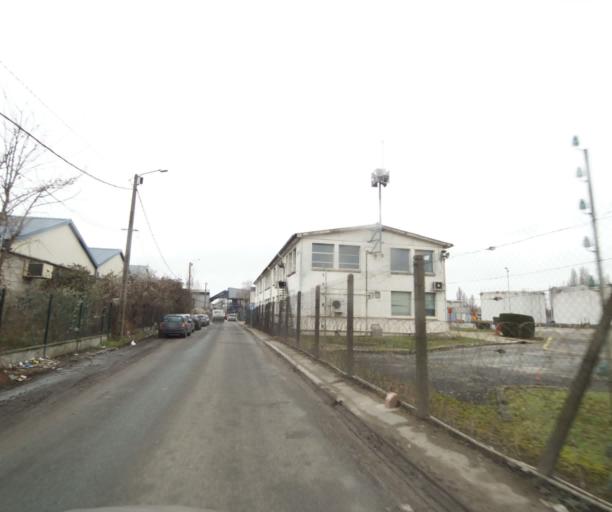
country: FR
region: Ile-de-France
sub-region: Departement du Val-de-Marne
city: Ablon-sur-Seine
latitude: 48.7369
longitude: 2.4310
